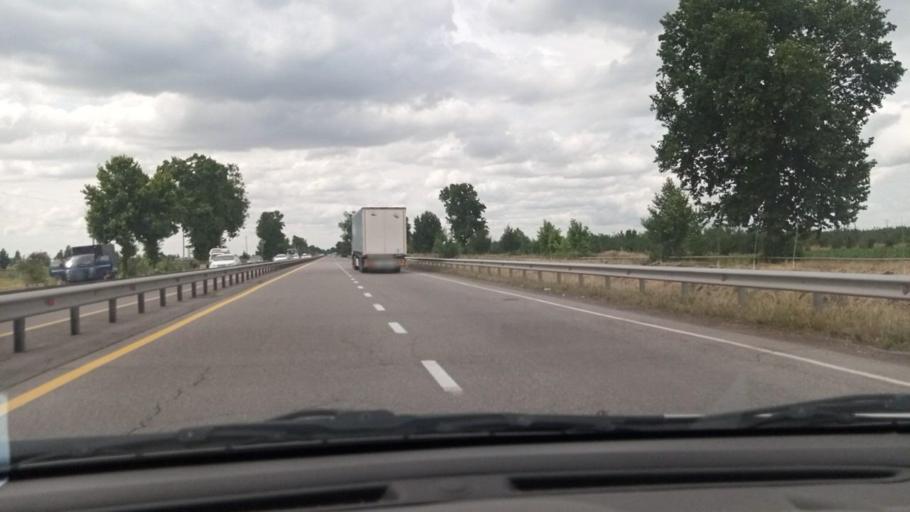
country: UZ
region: Toshkent Shahri
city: Bektemir
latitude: 41.1662
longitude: 69.4170
